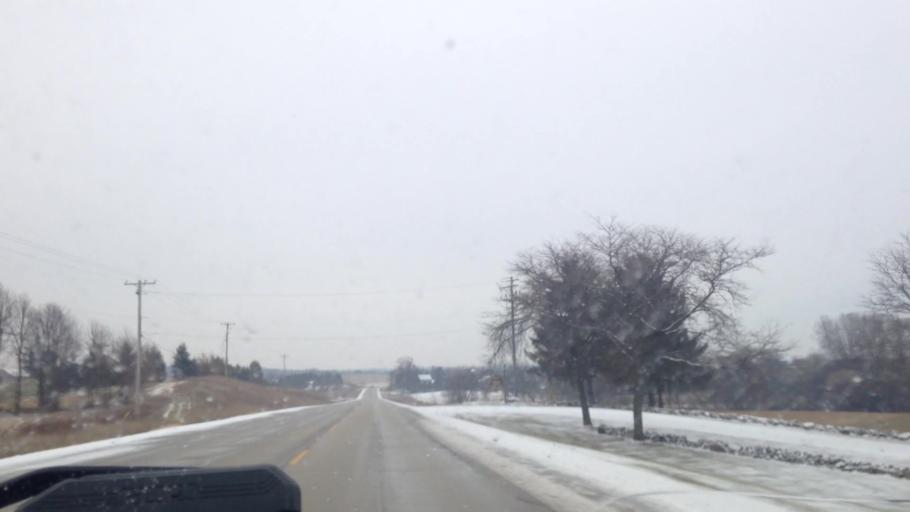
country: US
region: Wisconsin
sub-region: Dodge County
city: Hustisford
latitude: 43.2492
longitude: -88.5182
